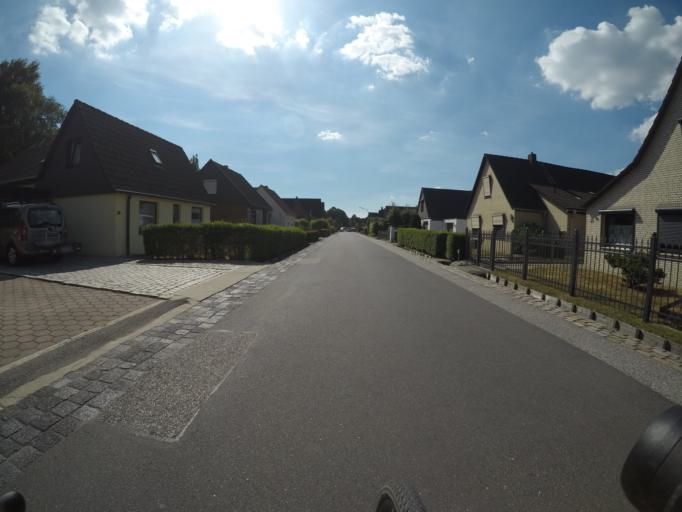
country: DE
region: Hamburg
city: Wandsbek
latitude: 53.5643
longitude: 10.1052
